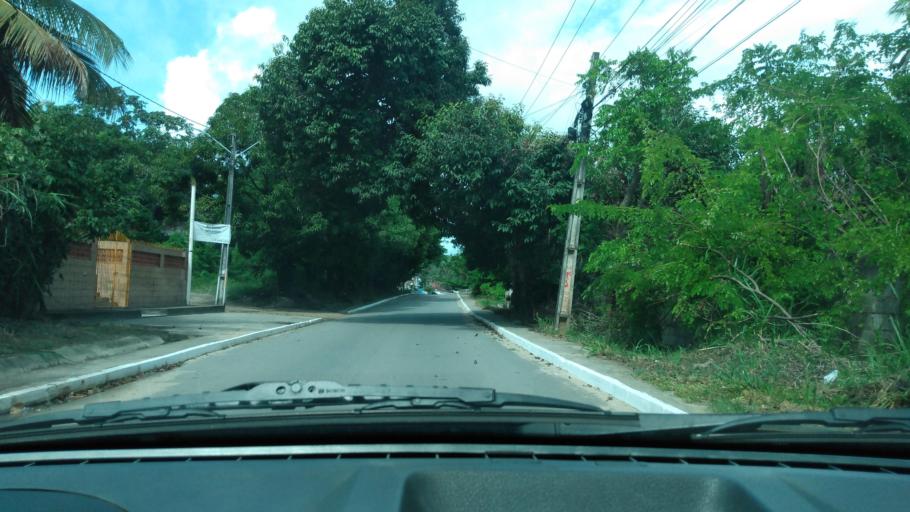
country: BR
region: Pernambuco
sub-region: Cabo De Santo Agostinho
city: Cabo
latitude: -8.3448
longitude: -34.9626
